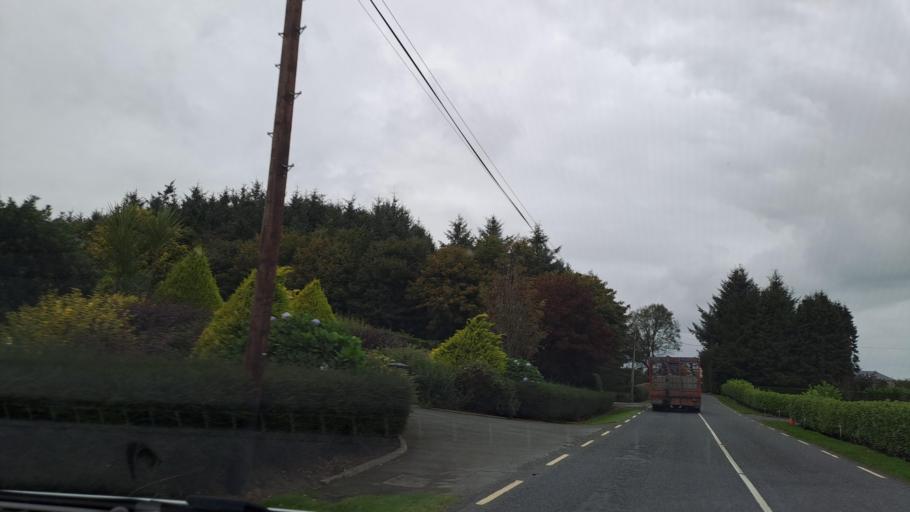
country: IE
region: Ulster
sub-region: County Monaghan
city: Castleblayney
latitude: 54.0862
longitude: -6.8279
